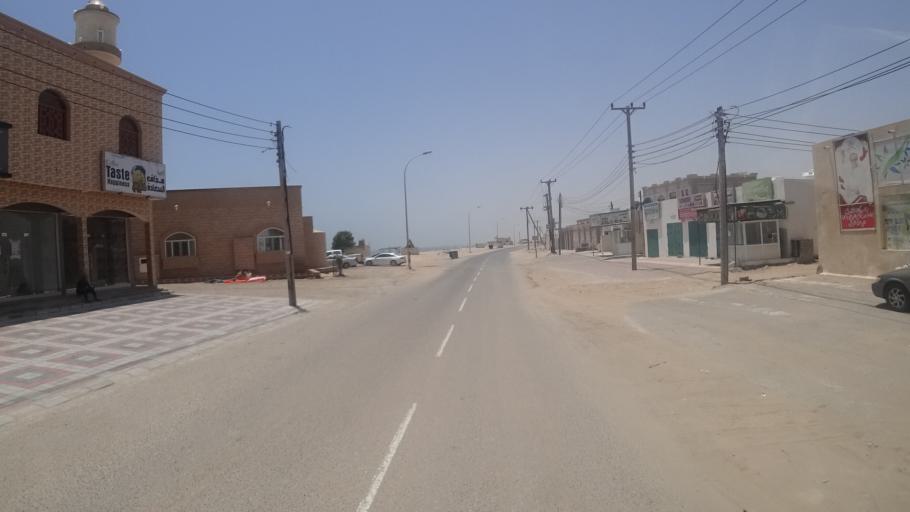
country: OM
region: Ash Sharqiyah
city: Sur
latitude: 22.0823
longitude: 59.6848
